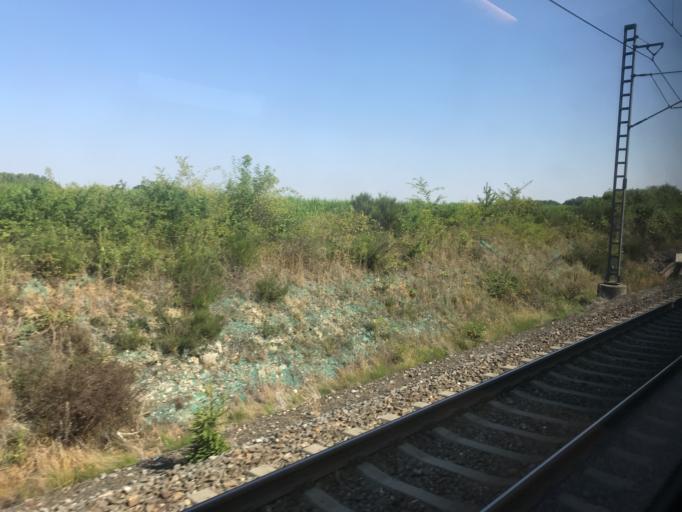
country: CZ
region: Central Bohemia
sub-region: Okres Praha-Vychod
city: Ricany
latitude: 49.9738
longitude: 14.6630
